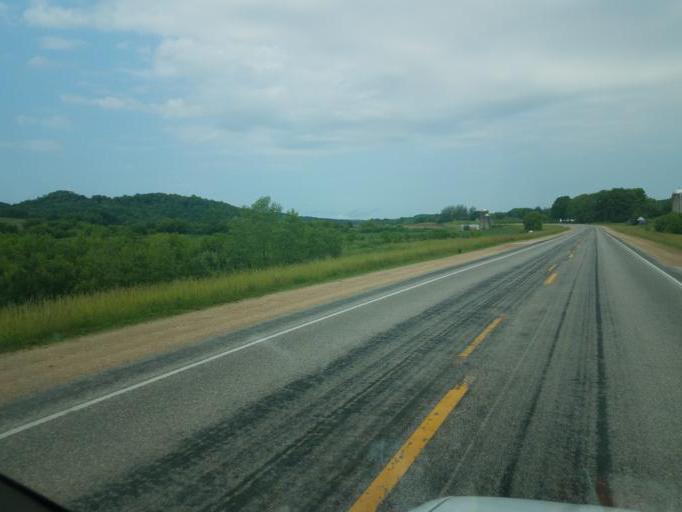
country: US
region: Wisconsin
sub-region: Vernon County
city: Hillsboro
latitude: 43.6590
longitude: -90.3720
